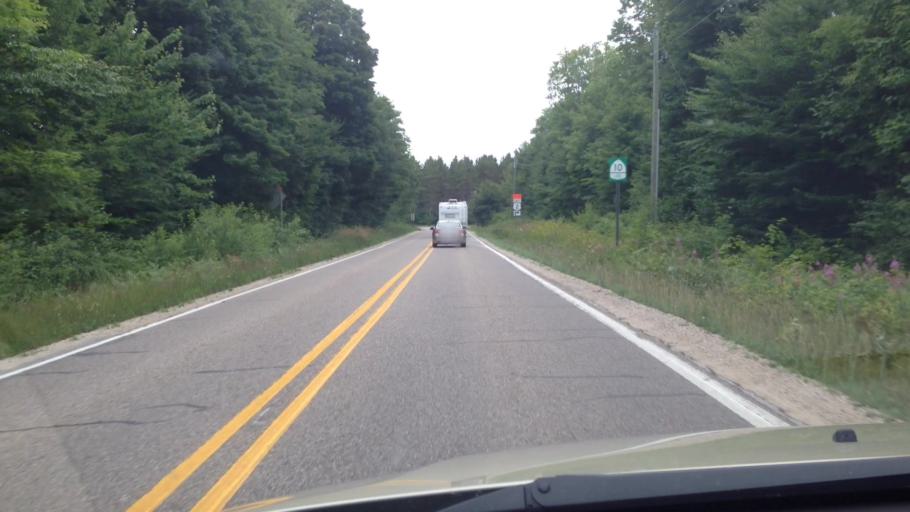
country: US
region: Michigan
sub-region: Mackinac County
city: Saint Ignace
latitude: 46.0547
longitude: -85.1508
